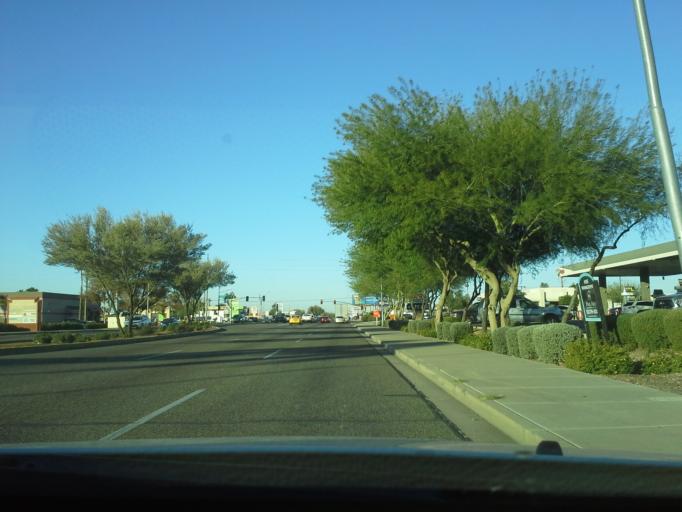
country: US
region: Arizona
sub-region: Maricopa County
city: Paradise Valley
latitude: 33.6407
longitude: -112.0113
